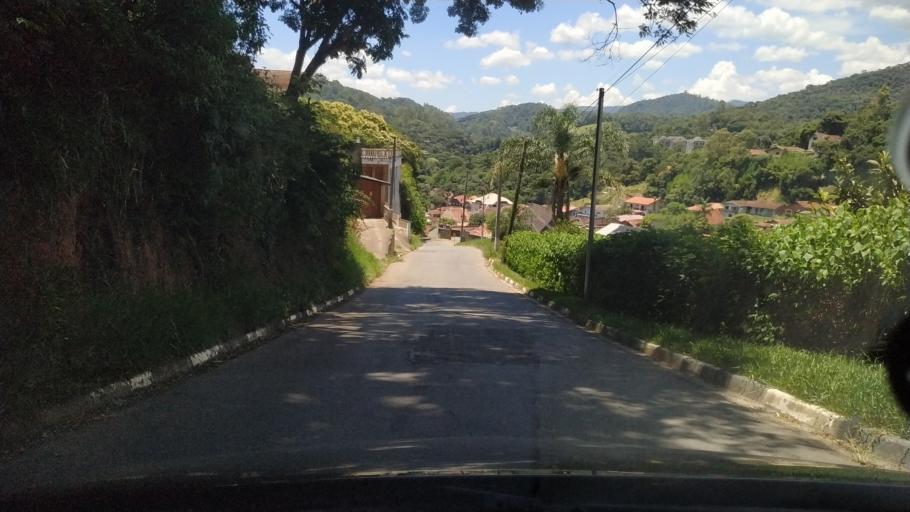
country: BR
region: Sao Paulo
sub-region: Campos Do Jordao
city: Campos do Jordao
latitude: -22.8294
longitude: -45.6669
